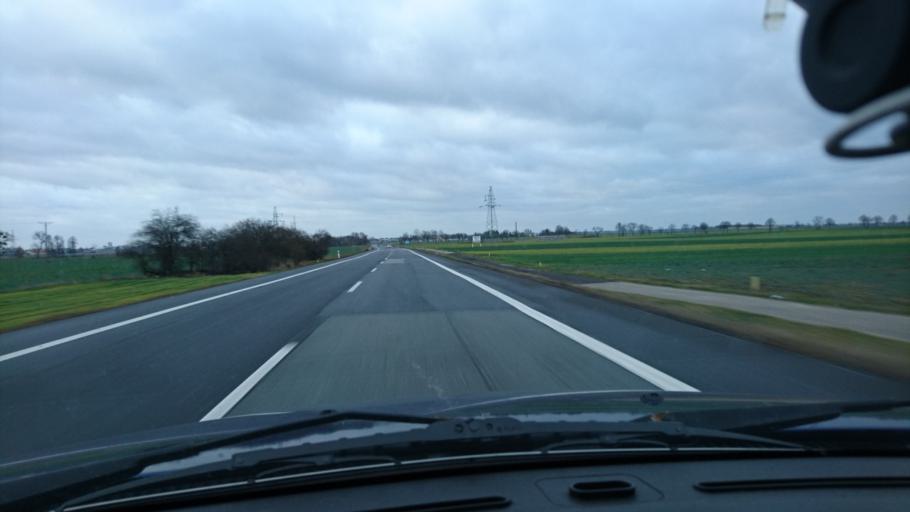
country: PL
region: Opole Voivodeship
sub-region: Powiat kluczborski
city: Kluczbork
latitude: 50.9900
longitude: 18.2268
